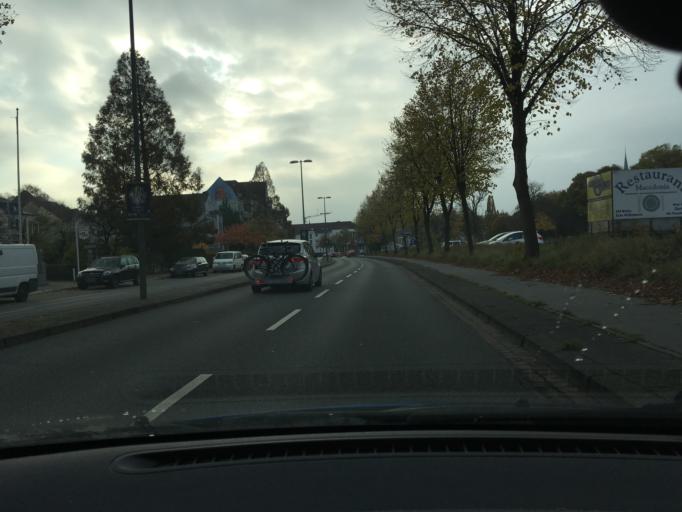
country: DE
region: Schleswig-Holstein
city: Flensburg
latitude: 54.7894
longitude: 9.4385
